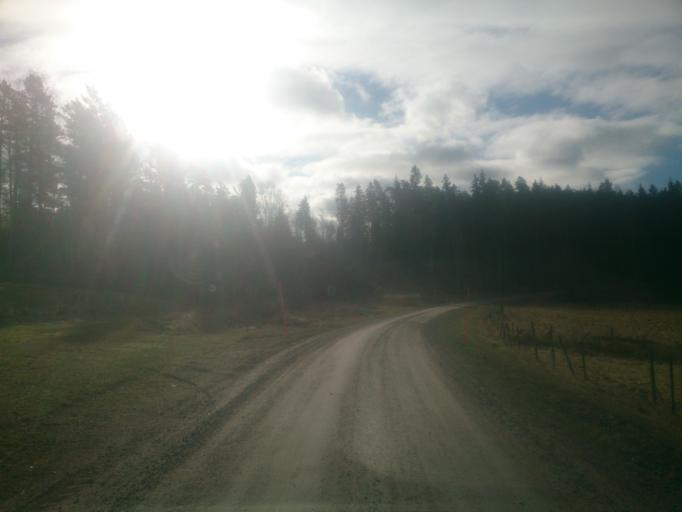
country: SE
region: OEstergoetland
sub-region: Atvidabergs Kommun
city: Atvidaberg
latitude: 58.2194
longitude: 16.1678
